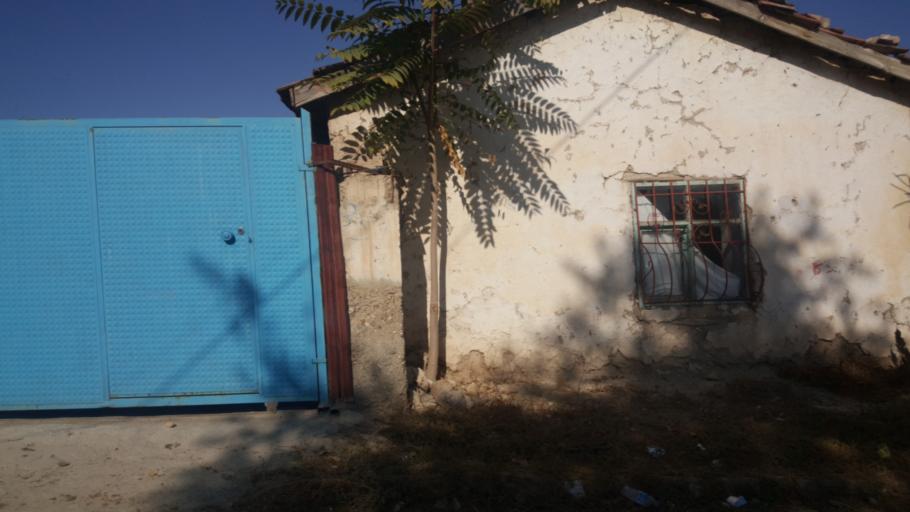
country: TR
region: Konya
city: Celtik
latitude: 39.0585
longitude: 31.8392
